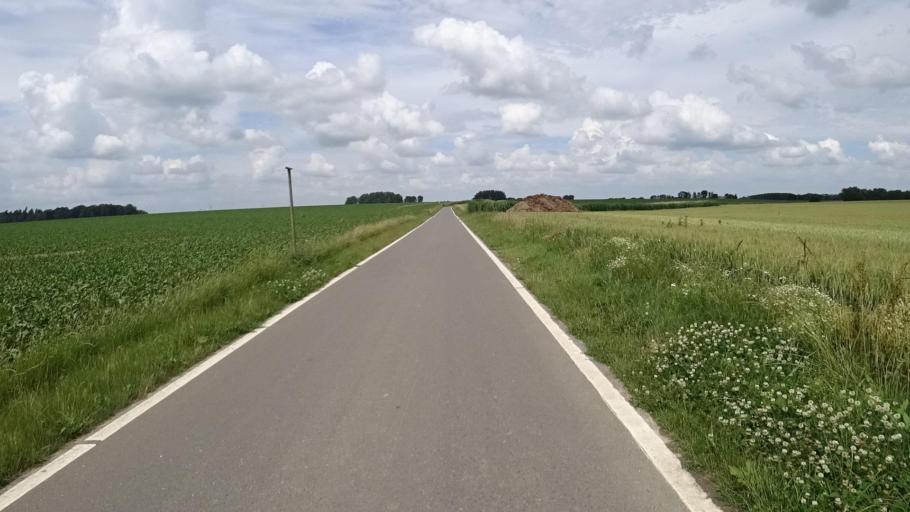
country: BE
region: Wallonia
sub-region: Province du Brabant Wallon
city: Perwez
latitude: 50.5502
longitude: 4.8322
